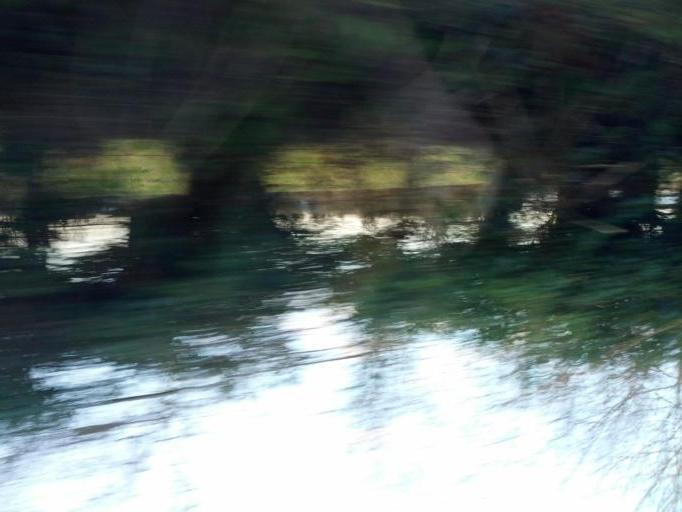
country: IE
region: Connaught
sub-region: County Galway
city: Loughrea
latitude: 53.3233
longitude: -8.6090
